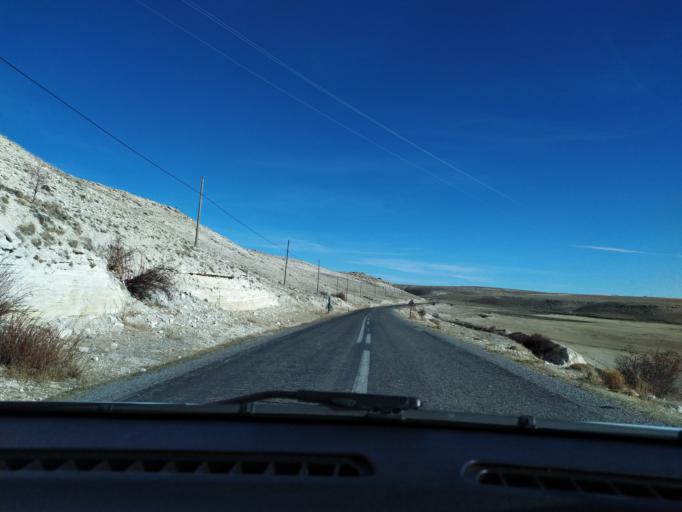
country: TR
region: Kayseri
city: Orensehir
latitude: 38.9785
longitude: 36.6652
